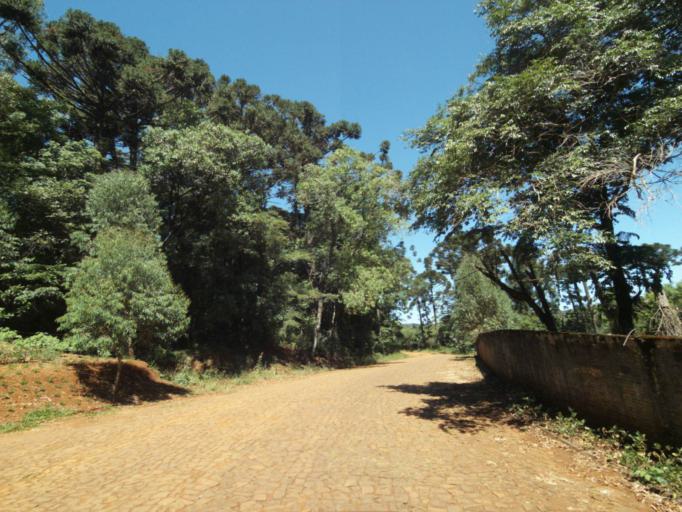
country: BR
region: Santa Catarina
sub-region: Sao Lourenco Do Oeste
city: Sao Lourenco dOeste
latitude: -26.2742
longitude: -52.7756
